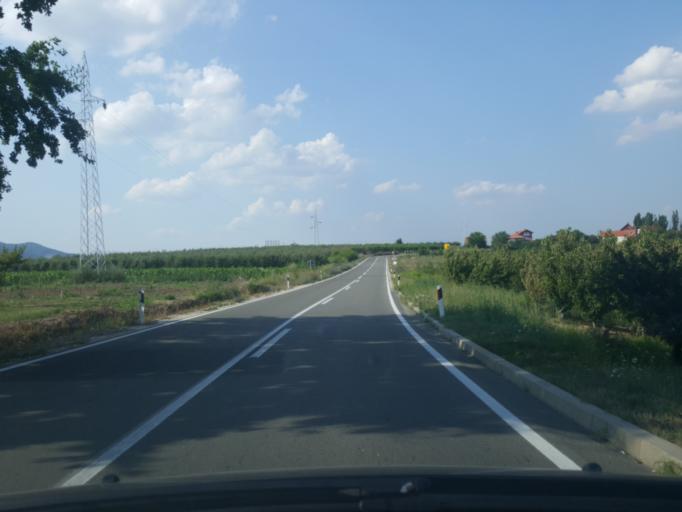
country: RS
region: Central Serbia
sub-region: Sumadijski Okrug
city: Topola
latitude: 44.2159
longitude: 20.6188
